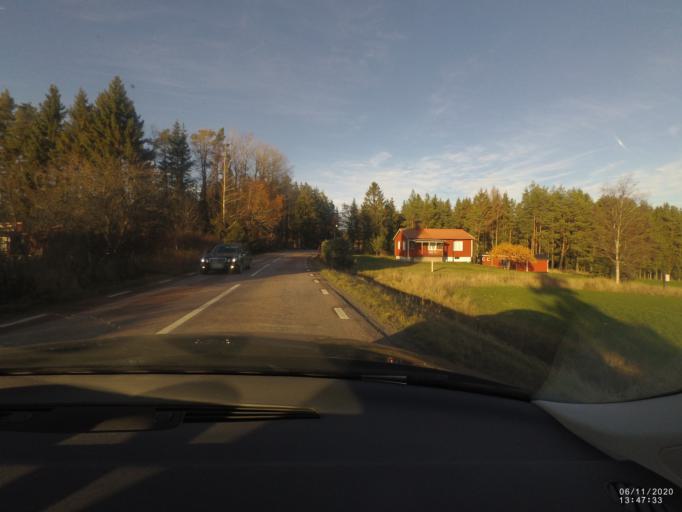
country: SE
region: Soedermanland
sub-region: Nykopings Kommun
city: Nykoping
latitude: 58.9003
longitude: 17.0924
